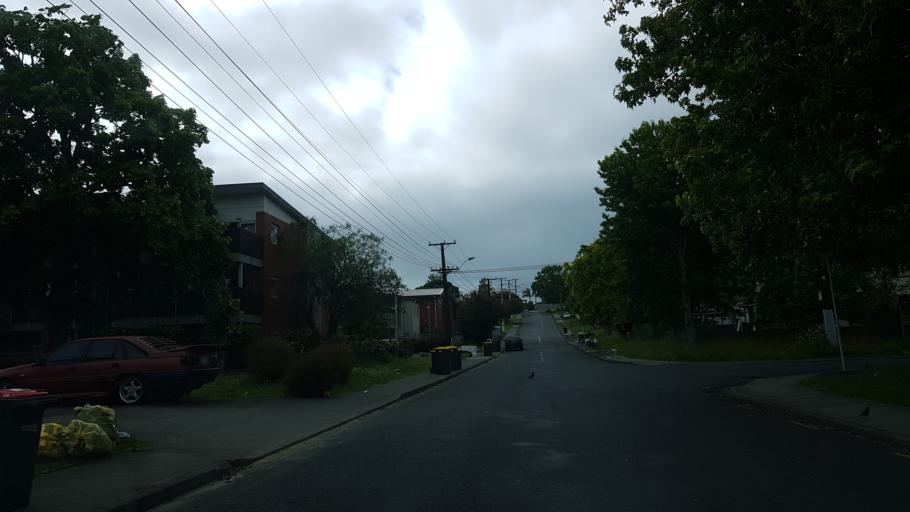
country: NZ
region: Auckland
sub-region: Auckland
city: North Shore
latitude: -36.7971
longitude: 174.7495
